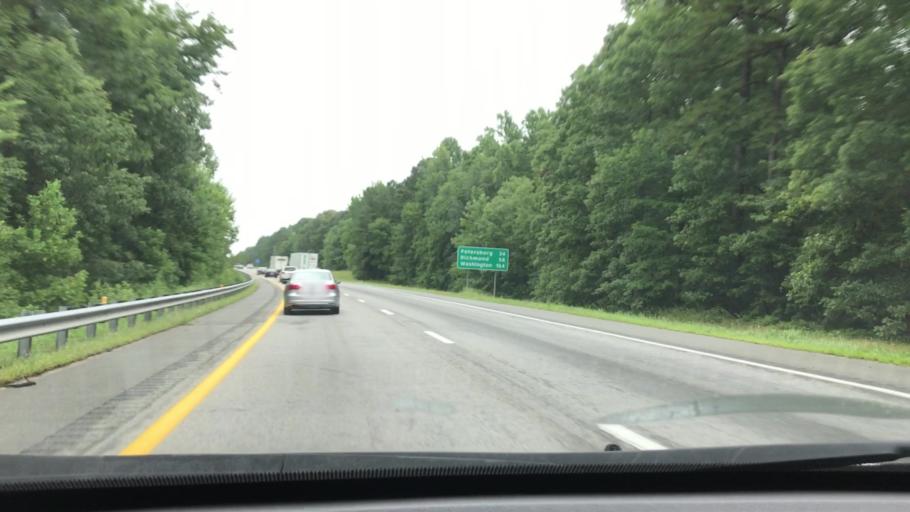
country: US
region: Virginia
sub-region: City of Emporia
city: Emporia
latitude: 36.7748
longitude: -77.4622
